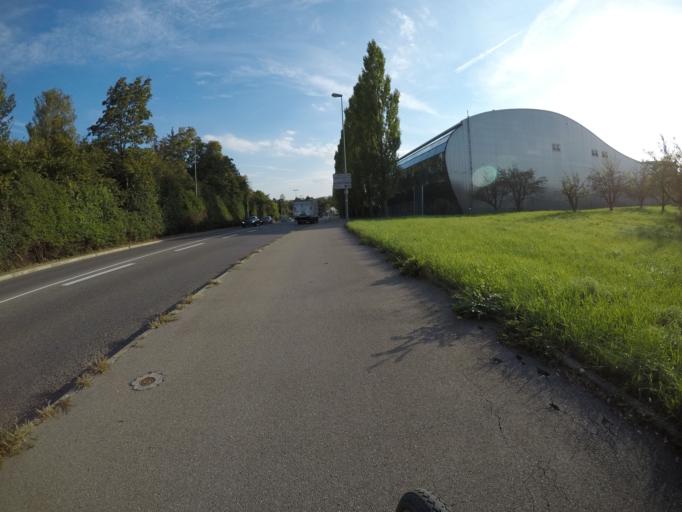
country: DE
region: Baden-Wuerttemberg
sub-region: Tuebingen Region
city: Sickenhausen
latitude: 48.5182
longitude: 9.2010
